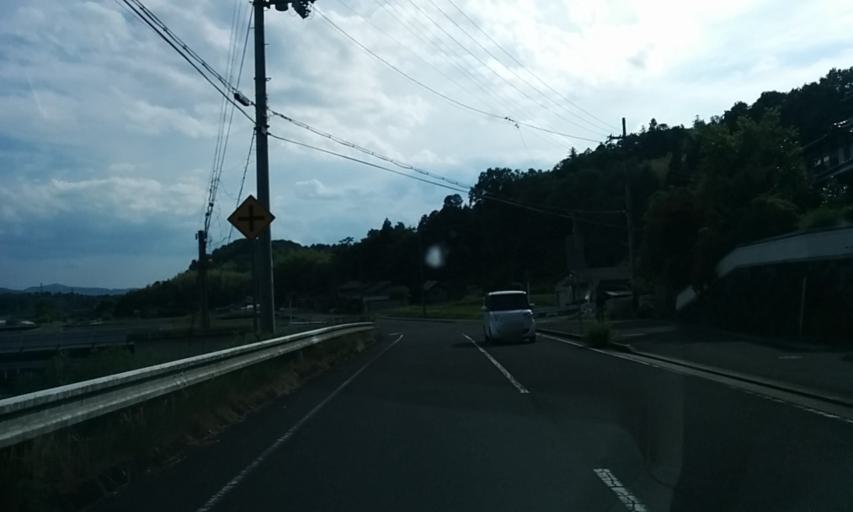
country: JP
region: Kyoto
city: Ayabe
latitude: 35.3385
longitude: 135.3049
